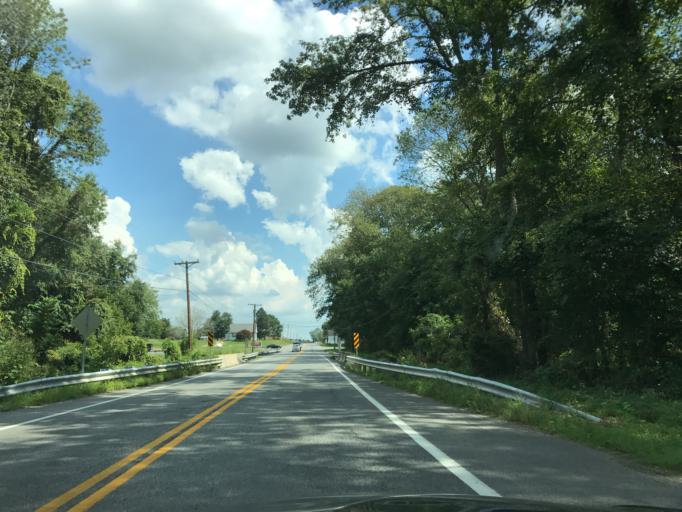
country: US
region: Maryland
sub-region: Queen Anne's County
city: Kingstown
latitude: 39.1841
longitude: -75.8949
